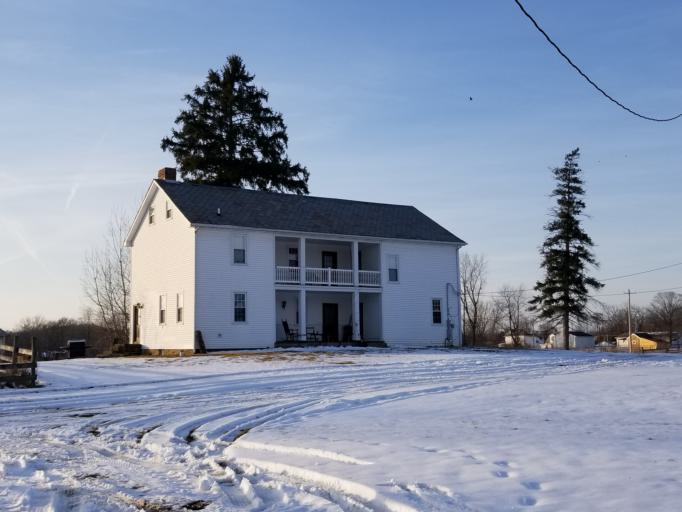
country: US
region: Ohio
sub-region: Licking County
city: Utica
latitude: 40.2278
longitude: -82.4376
